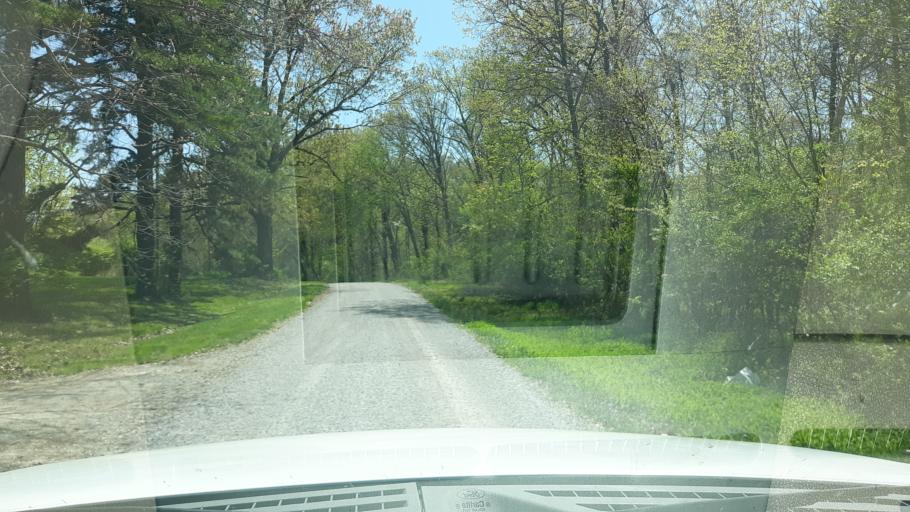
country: US
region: Illinois
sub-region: Saline County
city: Harrisburg
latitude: 37.8683
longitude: -88.6423
